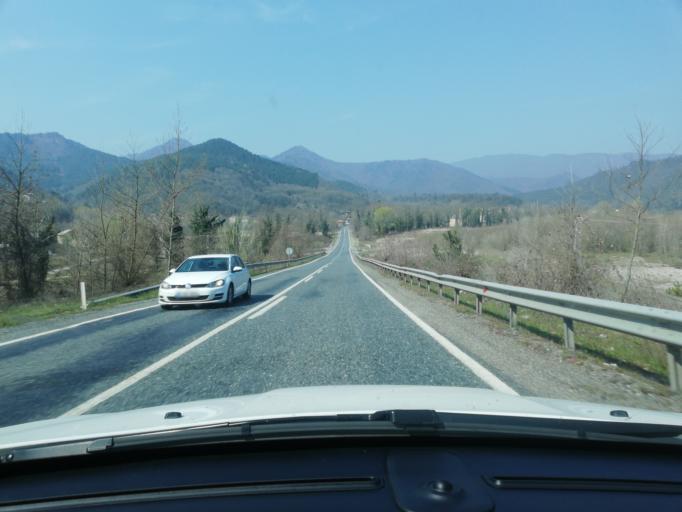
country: TR
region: Zonguldak
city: Gokcebey
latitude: 41.2307
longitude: 32.1993
